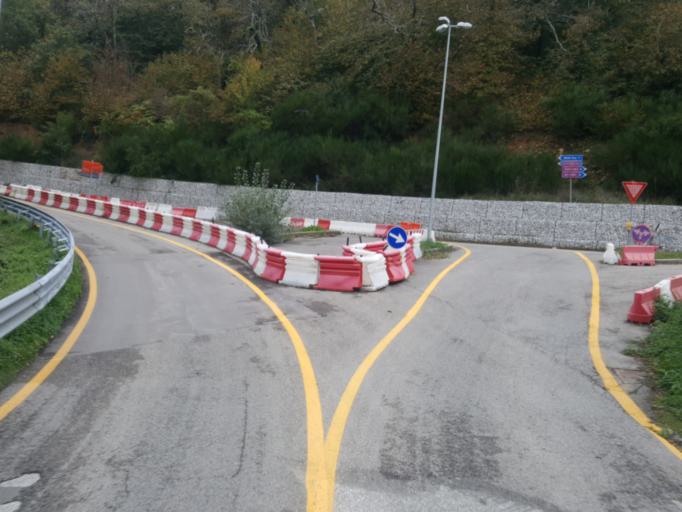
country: IT
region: Tuscany
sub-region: Province of Pisa
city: Castelnuovo di Val di Cecina
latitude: 43.2007
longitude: 10.9048
